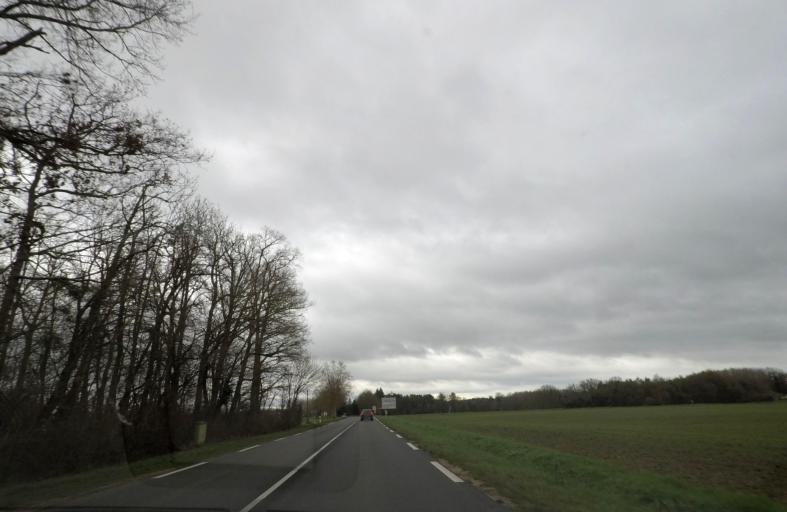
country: FR
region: Centre
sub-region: Departement du Loir-et-Cher
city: Cour-Cheverny
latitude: 47.5192
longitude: 1.4389
